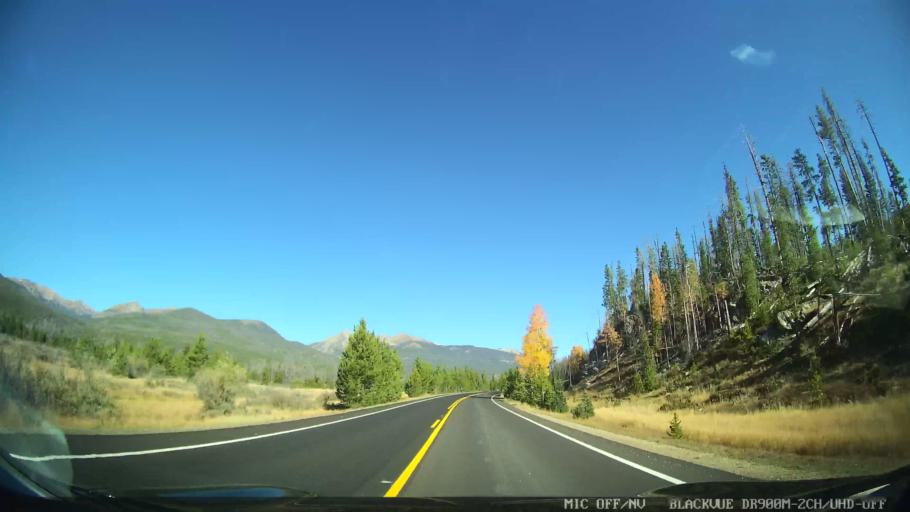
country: US
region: Colorado
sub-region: Grand County
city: Granby
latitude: 40.3258
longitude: -105.8533
